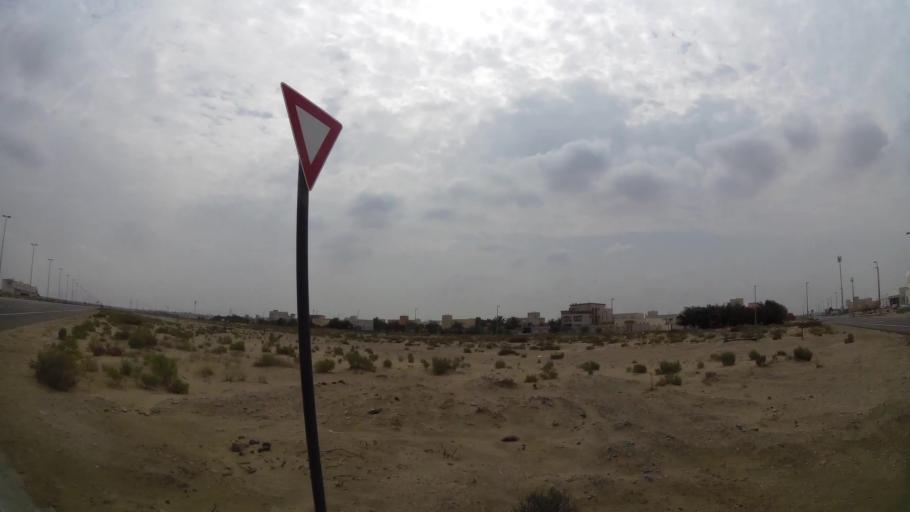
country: AE
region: Abu Dhabi
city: Abu Dhabi
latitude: 24.6381
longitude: 54.6717
